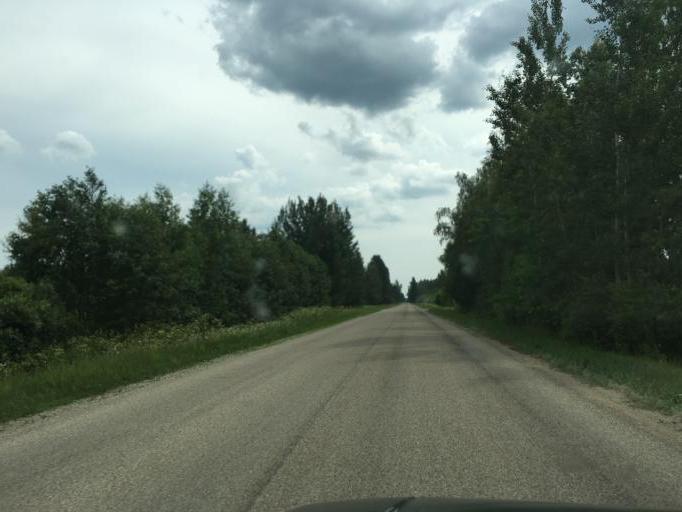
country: LV
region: Rugaju
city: Rugaji
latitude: 56.8331
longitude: 27.0937
